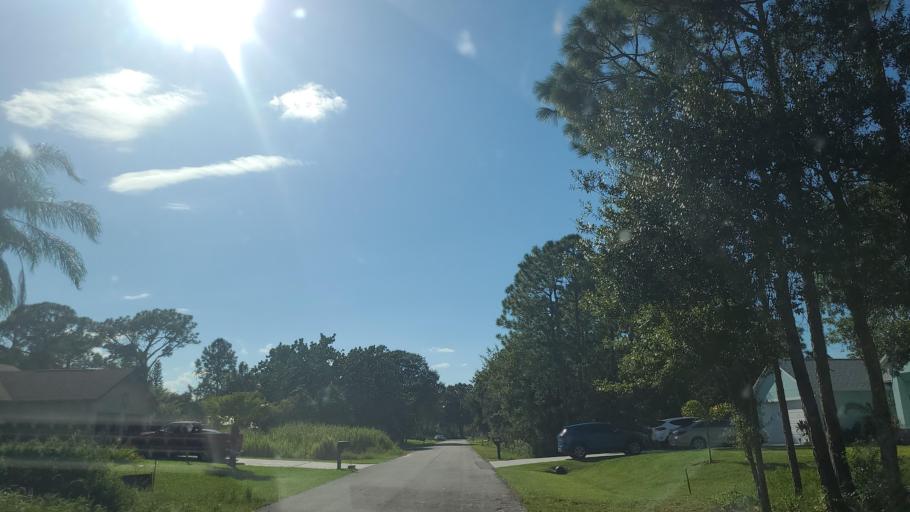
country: US
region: Florida
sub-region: Brevard County
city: Grant-Valkaria
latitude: 27.9645
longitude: -80.6238
